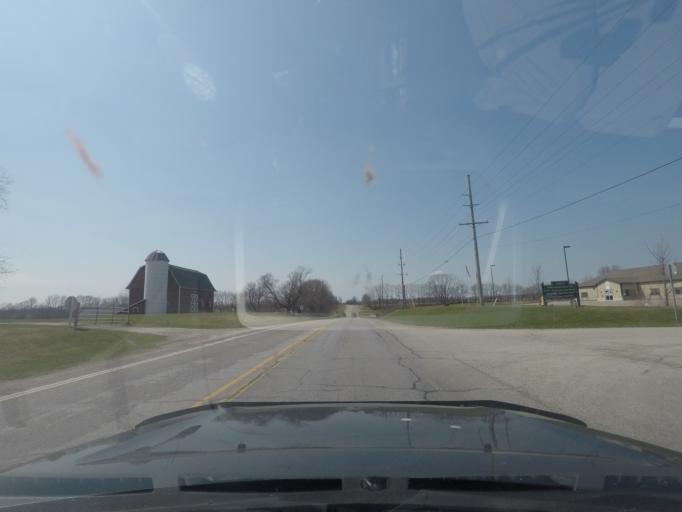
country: US
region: Indiana
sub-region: LaPorte County
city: LaPorte
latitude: 41.5912
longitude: -86.7524
